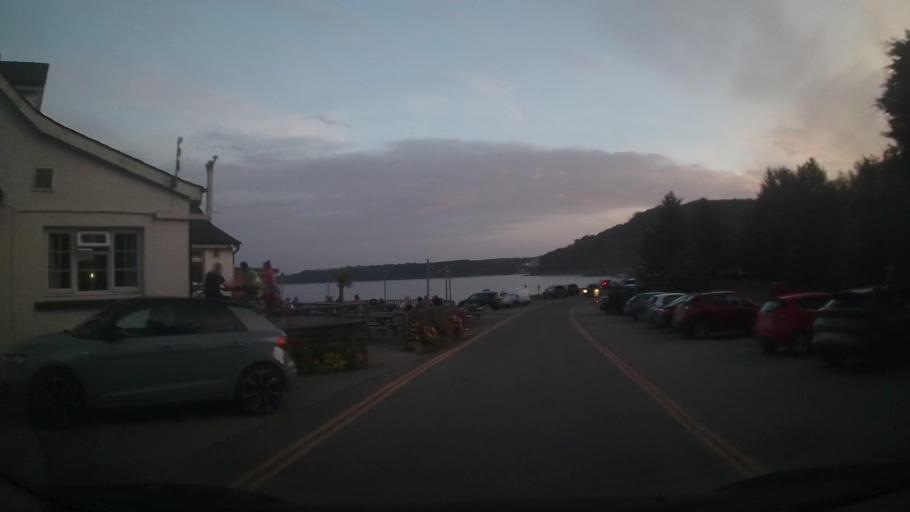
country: GB
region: Wales
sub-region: Pembrokeshire
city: Saundersfoot
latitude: 51.7245
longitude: -4.6841
